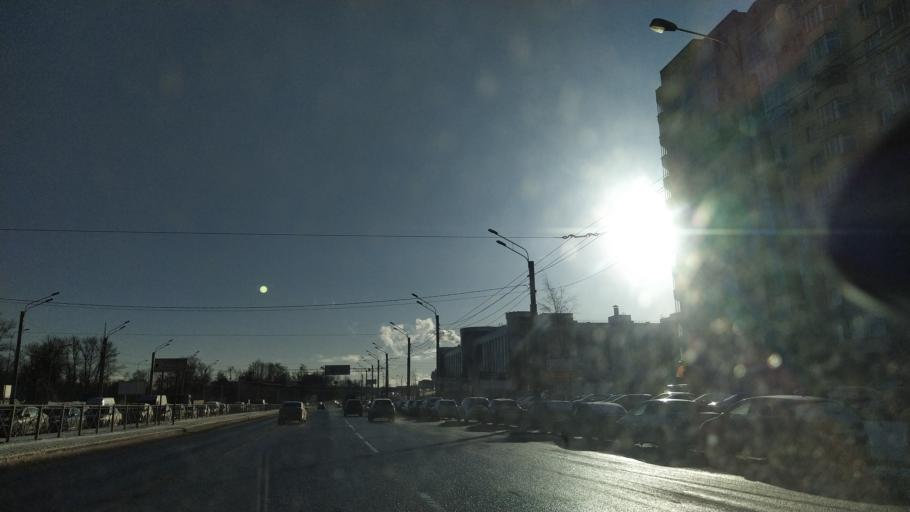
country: RU
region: Leningrad
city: Chernaya Rechka
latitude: 59.9984
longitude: 30.2992
